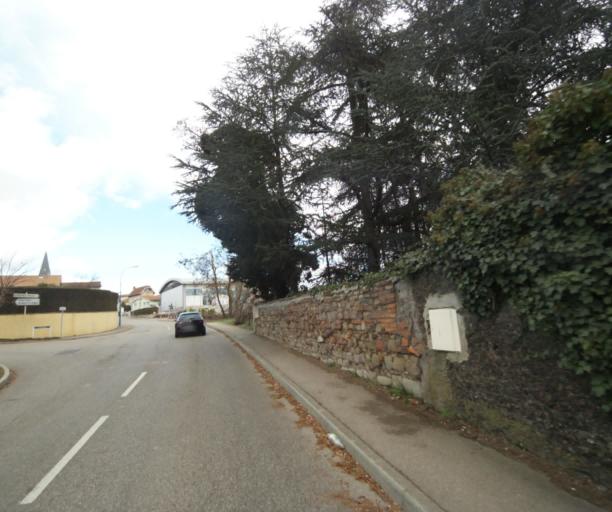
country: FR
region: Rhone-Alpes
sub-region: Departement de la Loire
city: La Talaudiere
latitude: 45.4770
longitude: 4.4288
